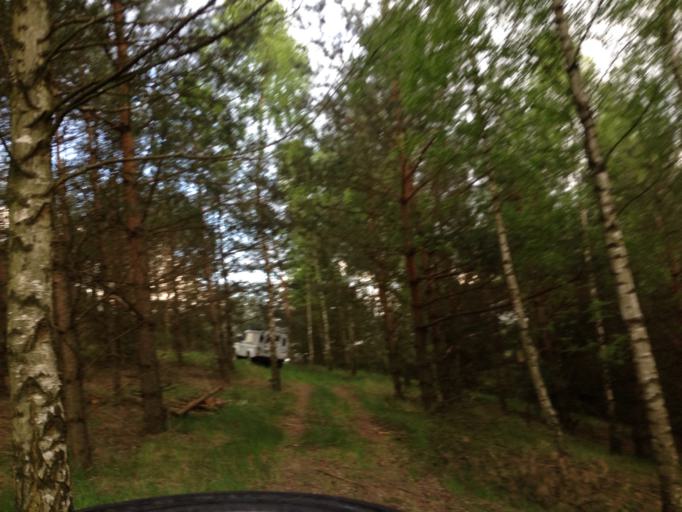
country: PL
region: Kujawsko-Pomorskie
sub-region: Powiat brodnicki
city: Bartniczka
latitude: 53.2800
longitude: 19.6585
